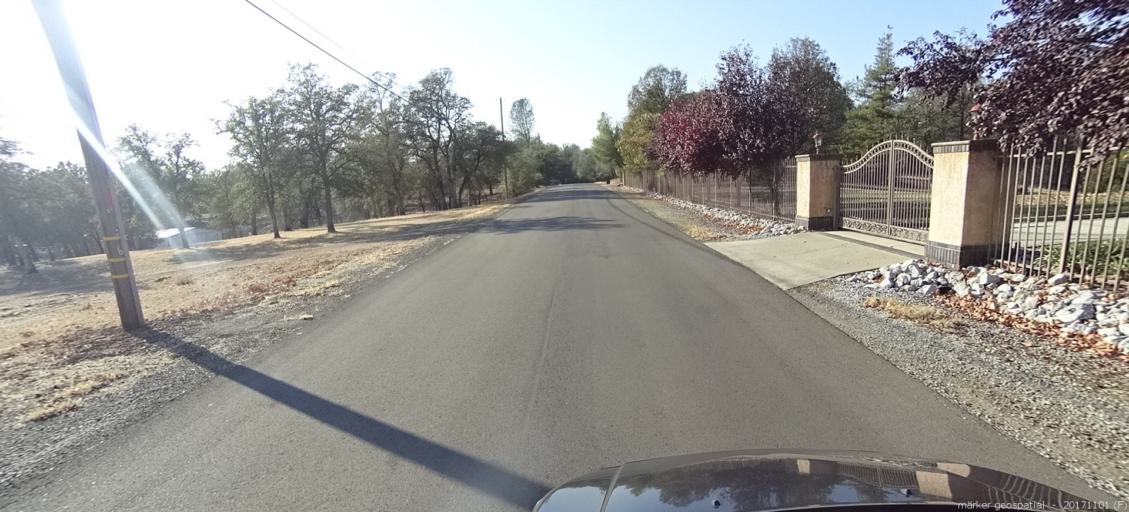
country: US
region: California
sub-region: Shasta County
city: Shasta Lake
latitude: 40.6760
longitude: -122.2984
